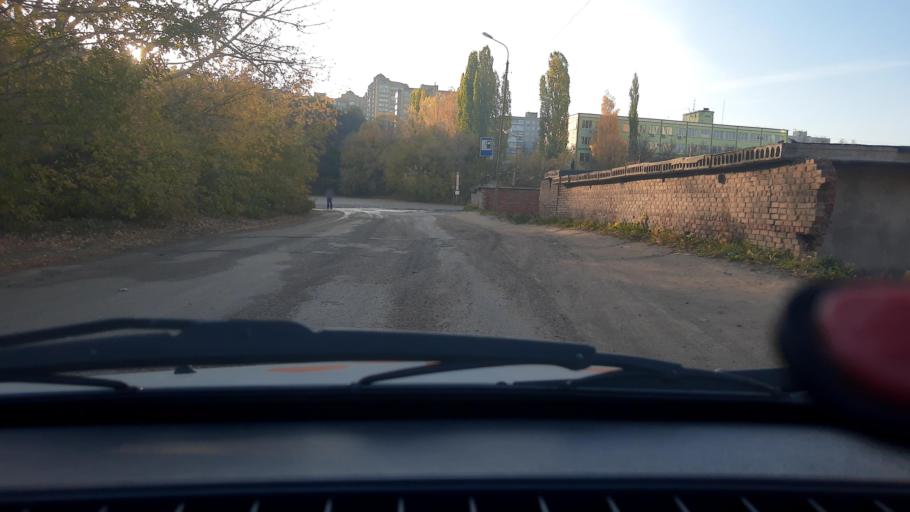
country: RU
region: Bashkortostan
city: Ufa
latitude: 54.7256
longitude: 55.9996
